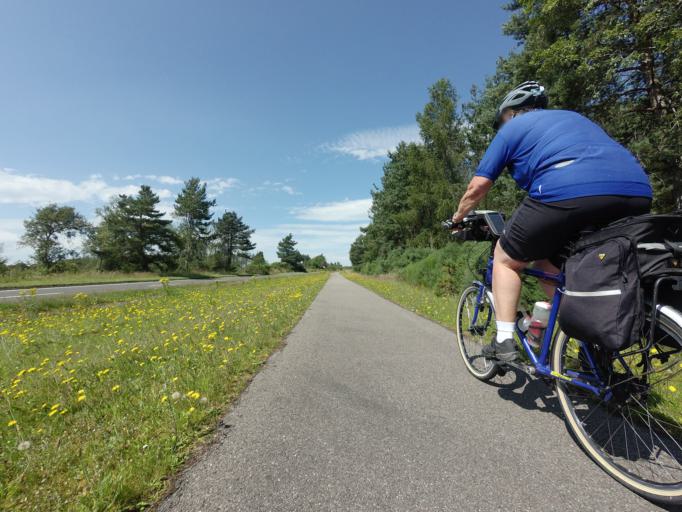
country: GB
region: Scotland
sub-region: Highland
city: Conon Bridge
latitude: 57.5401
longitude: -4.3722
